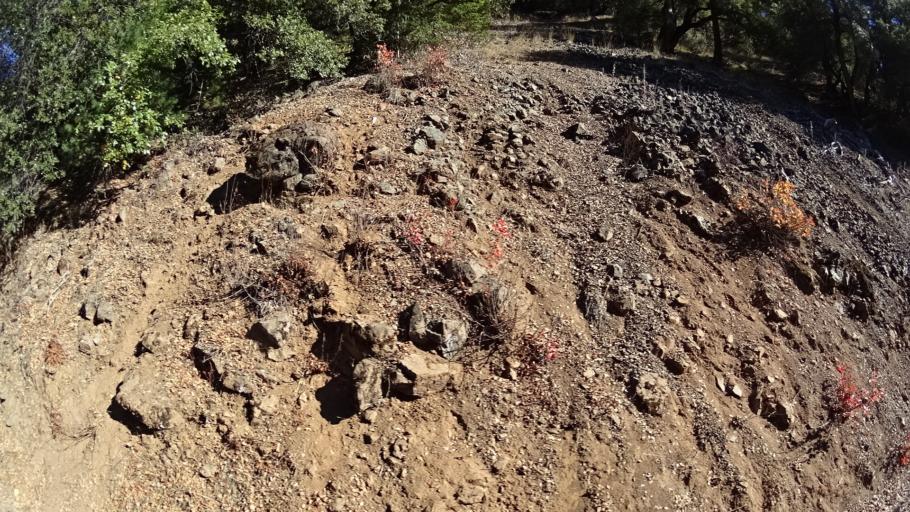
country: US
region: California
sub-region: Humboldt County
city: Willow Creek
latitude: 41.1993
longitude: -123.2202
